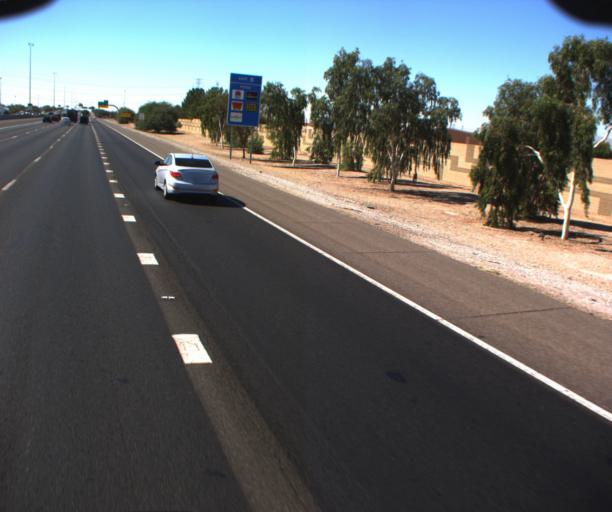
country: US
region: Arizona
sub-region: Maricopa County
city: Peoria
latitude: 33.5585
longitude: -112.2593
